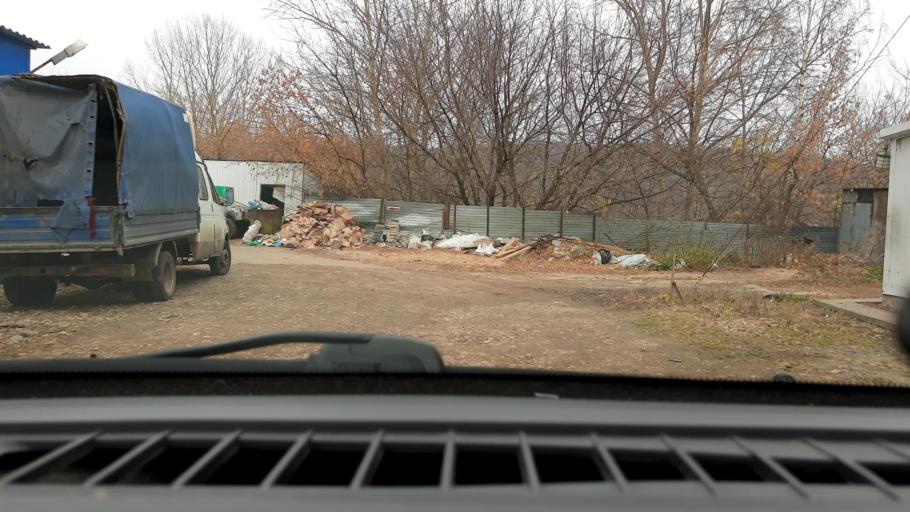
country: RU
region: Nizjnij Novgorod
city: Nizhniy Novgorod
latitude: 56.2838
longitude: 43.9575
